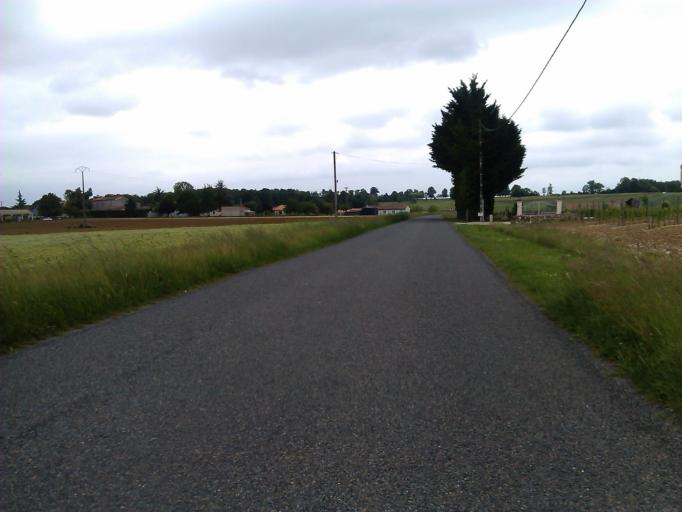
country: FR
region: Poitou-Charentes
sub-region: Departement de la Charente
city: Chateauneuf-sur-Charente
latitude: 45.5736
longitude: -0.0608
